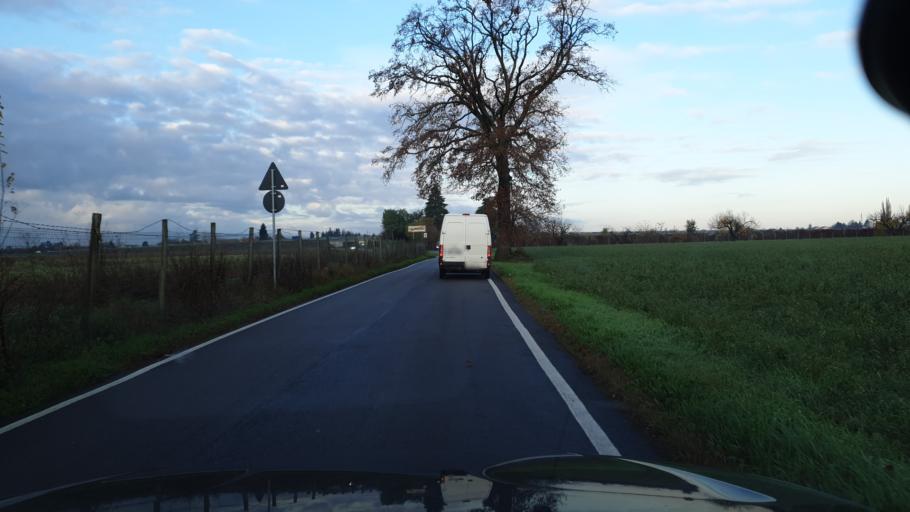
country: IT
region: Emilia-Romagna
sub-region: Provincia di Bologna
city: Crespellano
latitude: 44.5200
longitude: 11.1279
